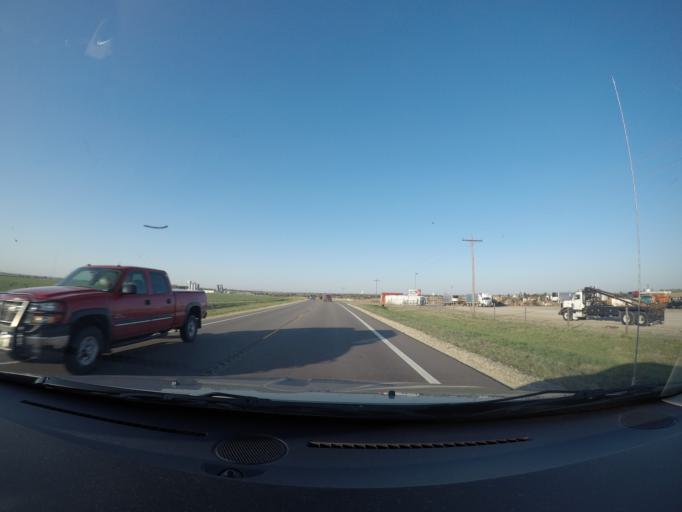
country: US
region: Kansas
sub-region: Pratt County
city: Pratt
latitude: 37.6716
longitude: -98.7140
